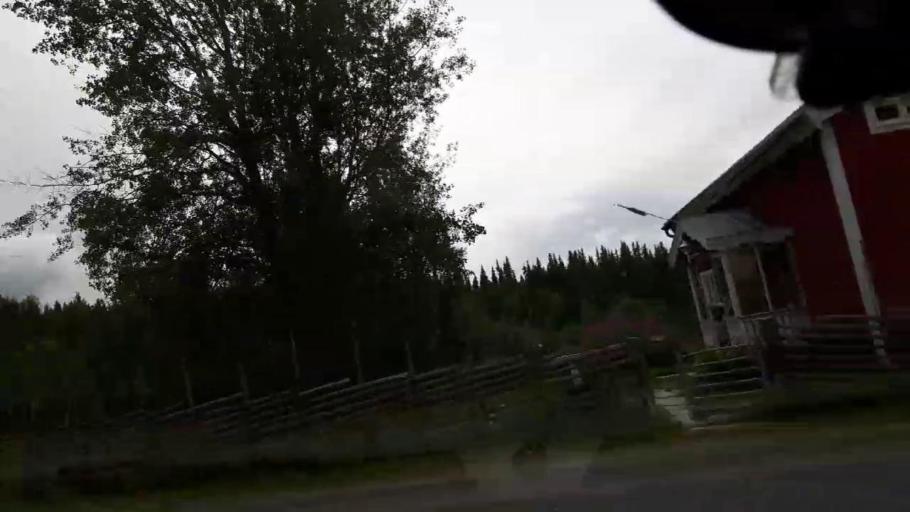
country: SE
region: Jaemtland
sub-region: Krokoms Kommun
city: Valla
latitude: 63.7793
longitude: 13.8165
